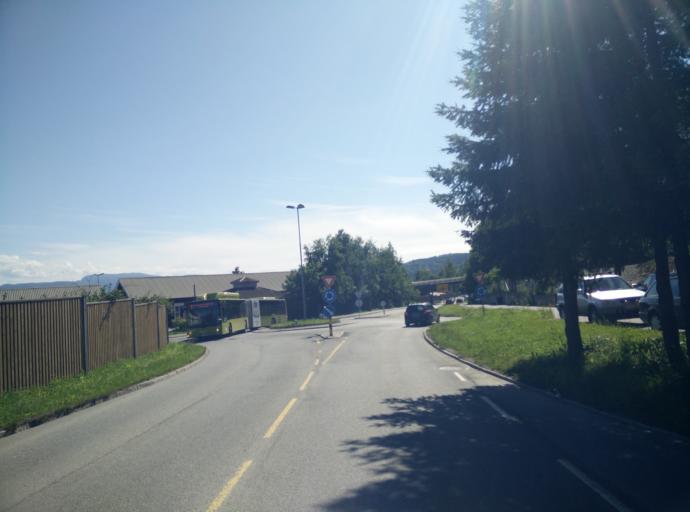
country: NO
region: Sor-Trondelag
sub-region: Trondheim
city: Trondheim
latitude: 63.3986
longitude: 10.3577
